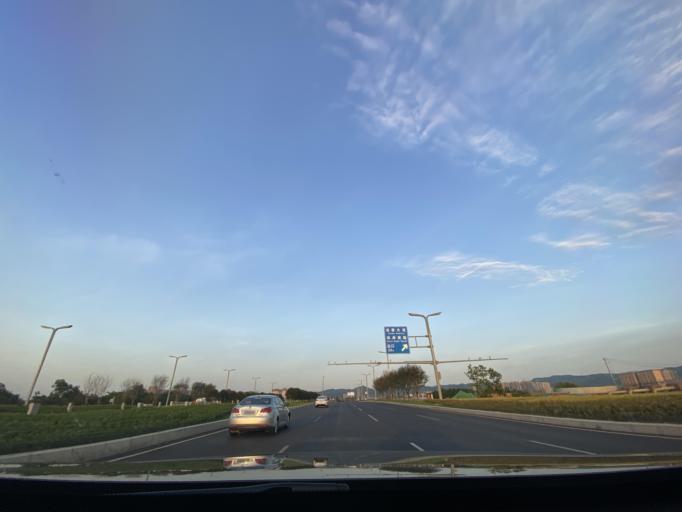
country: CN
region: Sichuan
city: Longquan
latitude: 30.5998
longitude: 104.2658
